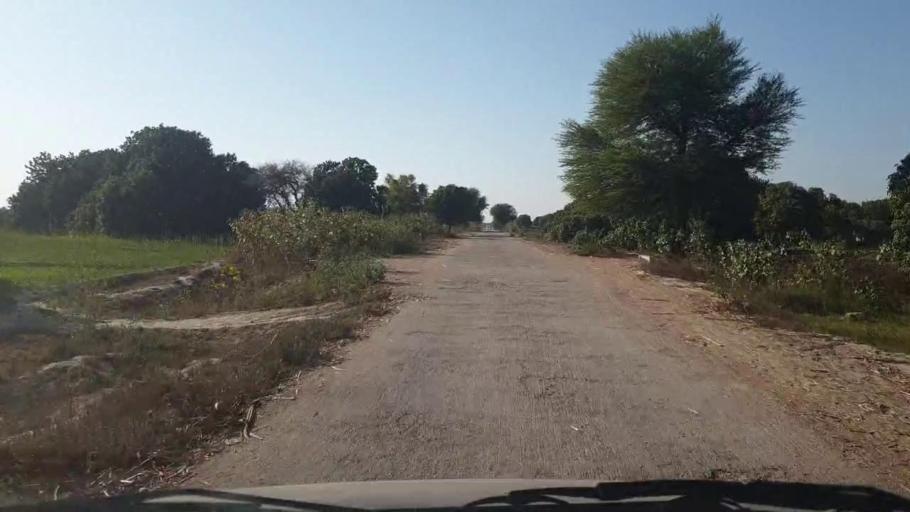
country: PK
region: Sindh
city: Samaro
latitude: 25.3570
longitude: 69.3032
